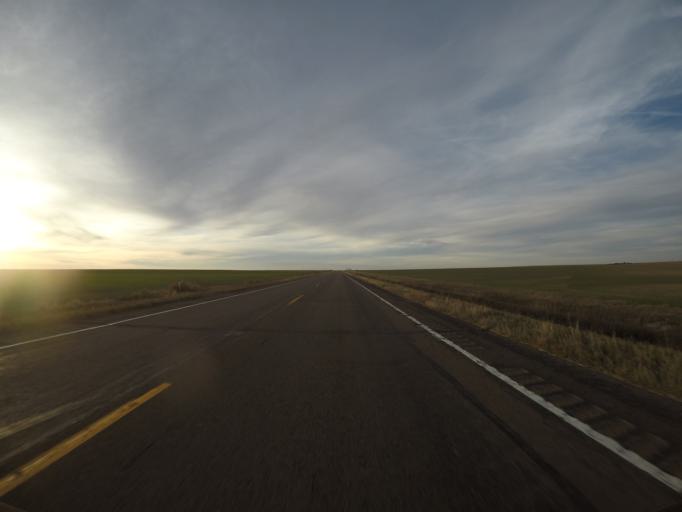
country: US
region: Colorado
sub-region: Washington County
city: Akron
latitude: 39.7319
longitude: -103.1667
